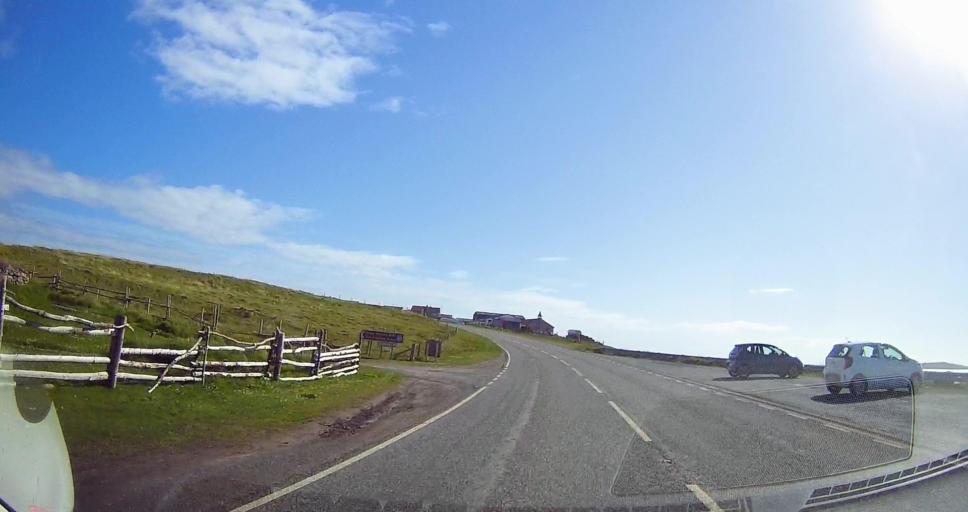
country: GB
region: Scotland
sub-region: Shetland Islands
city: Sandwick
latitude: 59.8793
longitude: -1.3064
